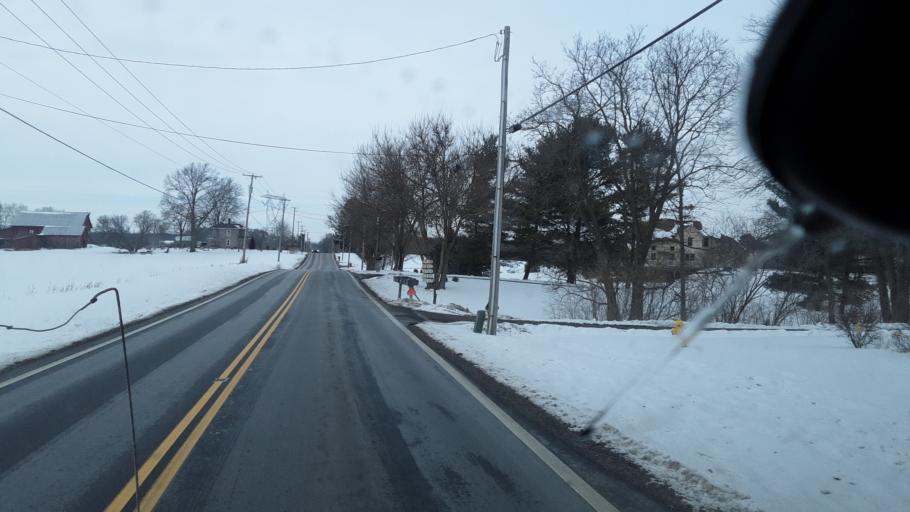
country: US
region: Ohio
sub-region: Delaware County
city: Powell
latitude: 40.2259
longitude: -83.1505
